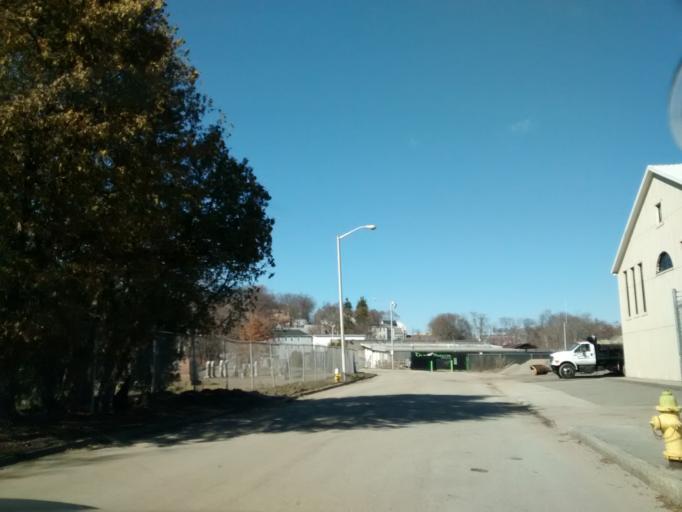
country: US
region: Massachusetts
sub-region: Worcester County
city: Worcester
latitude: 42.2810
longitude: -71.7995
